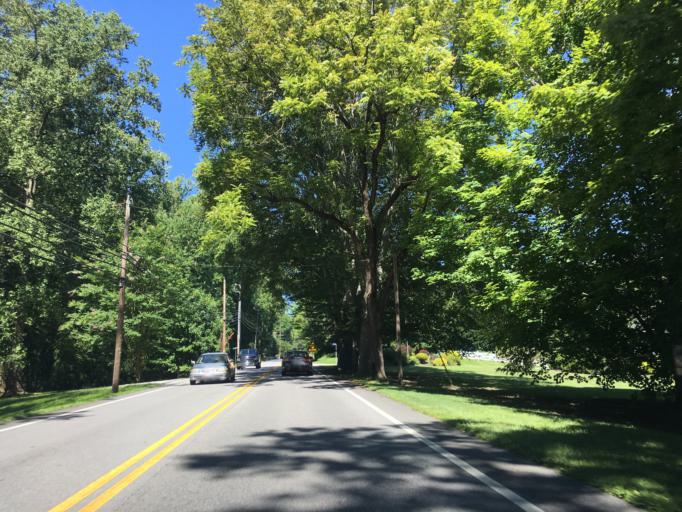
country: US
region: Maryland
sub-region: Anne Arundel County
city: Crownsville
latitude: 39.0474
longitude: -76.6113
